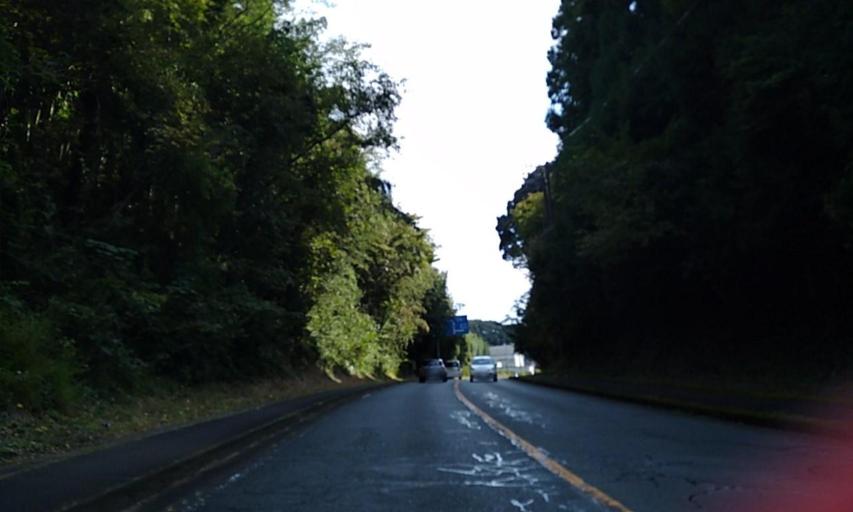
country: JP
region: Shizuoka
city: Mori
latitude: 34.8237
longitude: 137.9025
